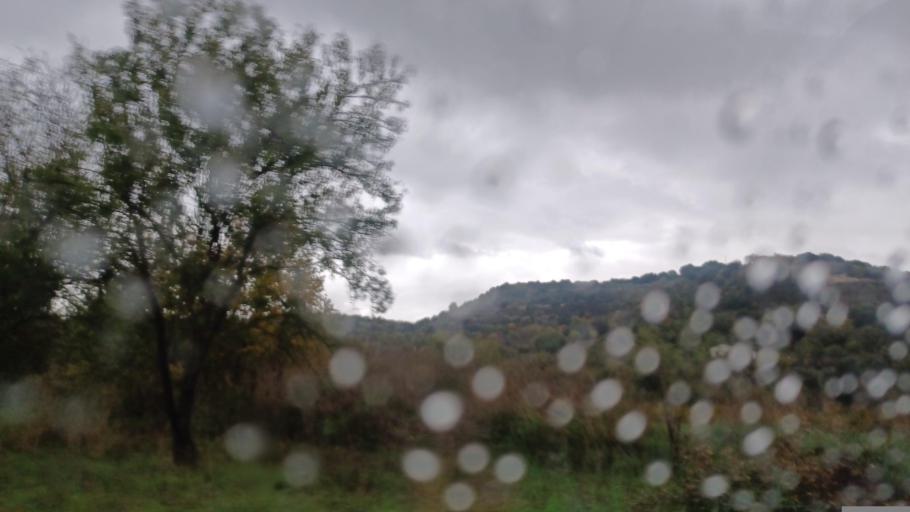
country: CY
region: Pafos
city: Mesogi
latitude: 34.8734
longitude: 32.5487
